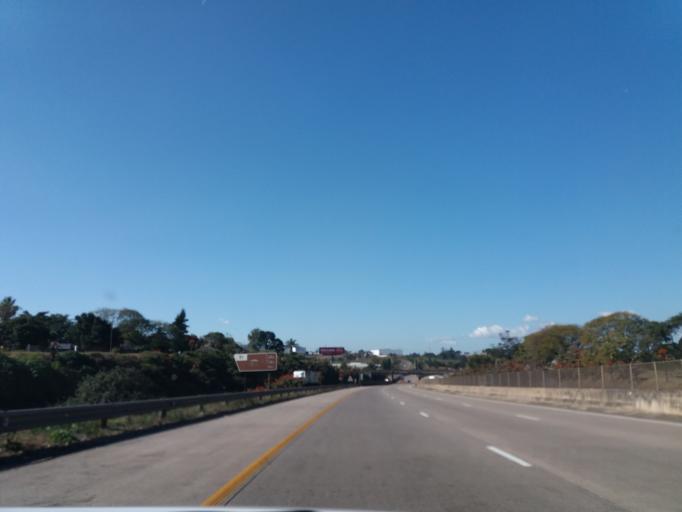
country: ZA
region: KwaZulu-Natal
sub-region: uMgungundlovu District Municipality
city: Camperdown
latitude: -29.7324
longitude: 30.5914
